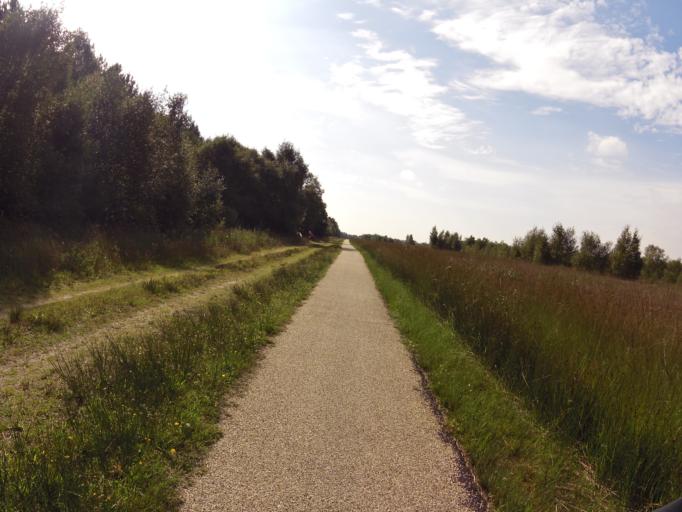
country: DE
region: Lower Saxony
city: Twist
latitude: 52.6690
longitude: 7.0575
